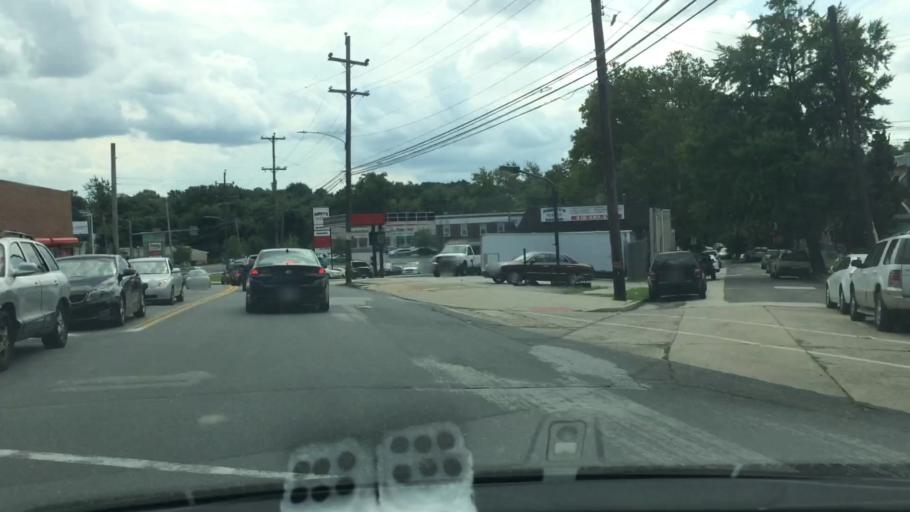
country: US
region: Pennsylvania
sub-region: Delaware County
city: Darby
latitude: 39.9212
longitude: -75.2640
